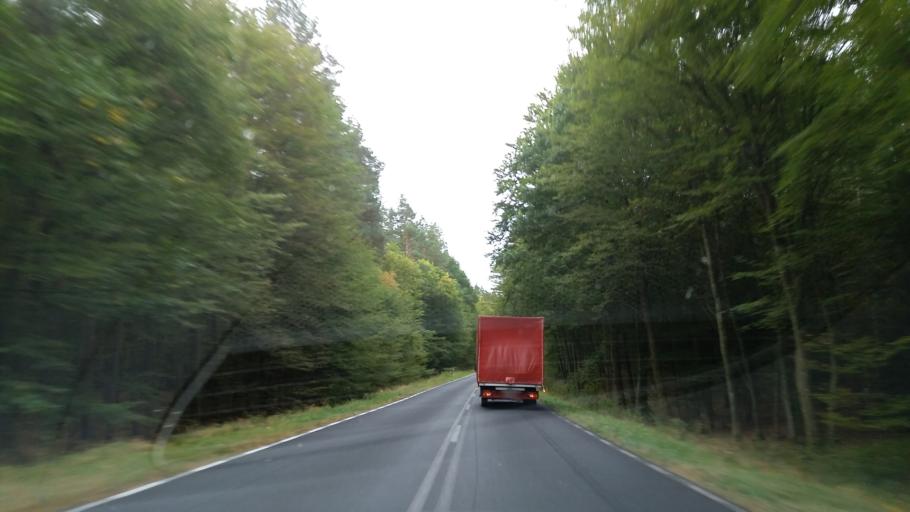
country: PL
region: West Pomeranian Voivodeship
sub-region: Powiat mysliborski
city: Barlinek
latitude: 52.9339
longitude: 15.1934
